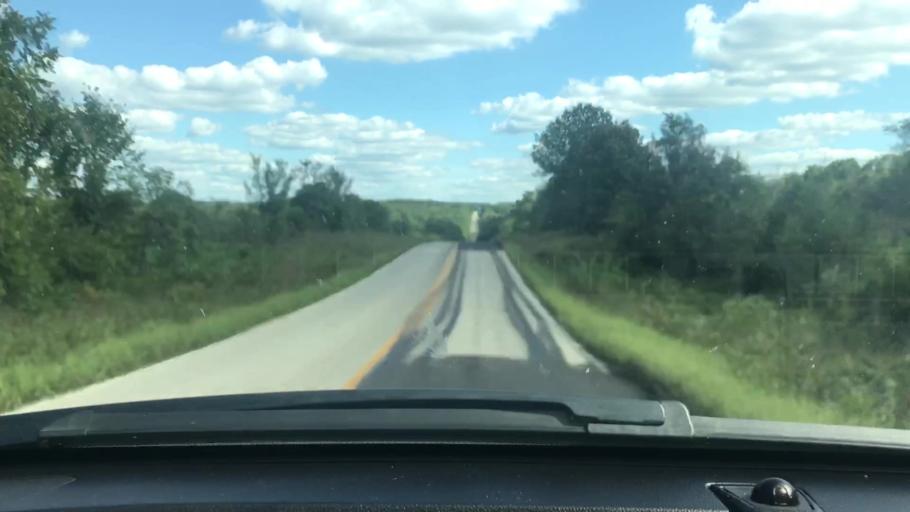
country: US
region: Missouri
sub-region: Wright County
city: Hartville
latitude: 37.3883
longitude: -92.4459
